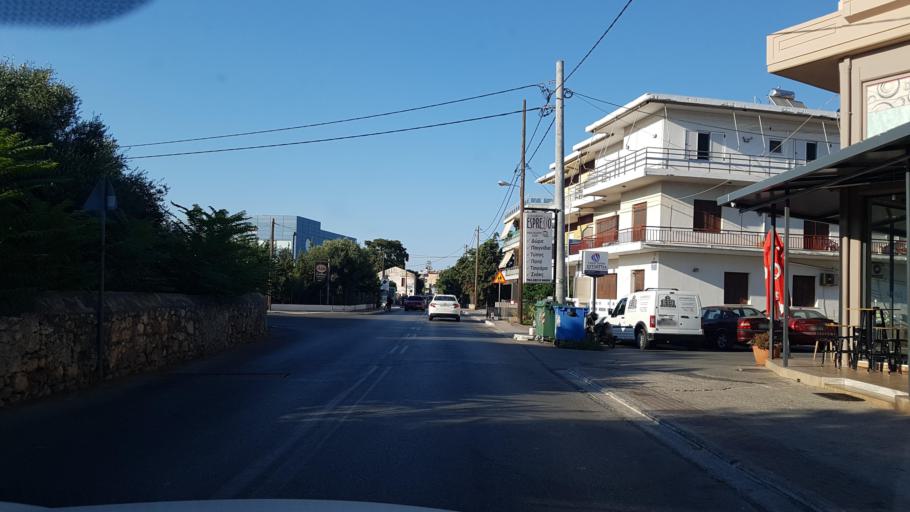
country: GR
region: Crete
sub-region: Nomos Chanias
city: Mournies
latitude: 35.5044
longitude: 24.0070
